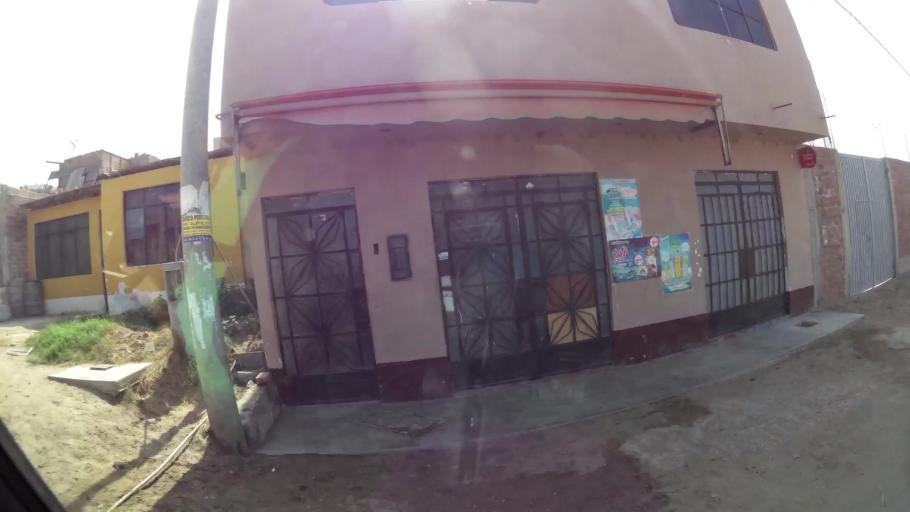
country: PE
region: Lima
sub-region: Lima
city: Santa Rosa
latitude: -11.7842
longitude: -77.1621
